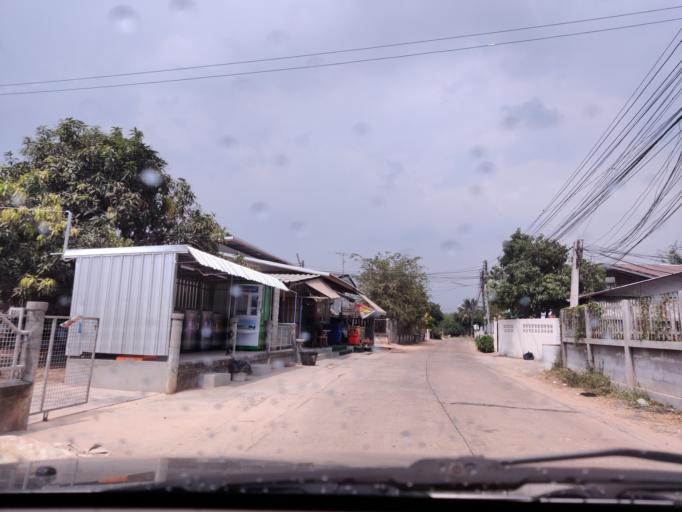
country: TH
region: Sisaket
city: Si Sa Ket
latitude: 15.1045
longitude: 104.3542
